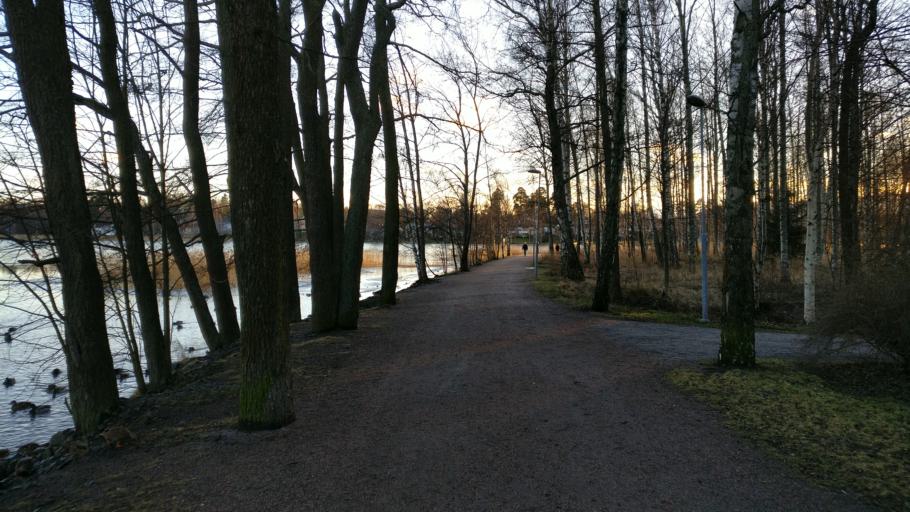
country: FI
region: Uusimaa
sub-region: Helsinki
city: Vantaa
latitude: 60.1898
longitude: 25.0480
